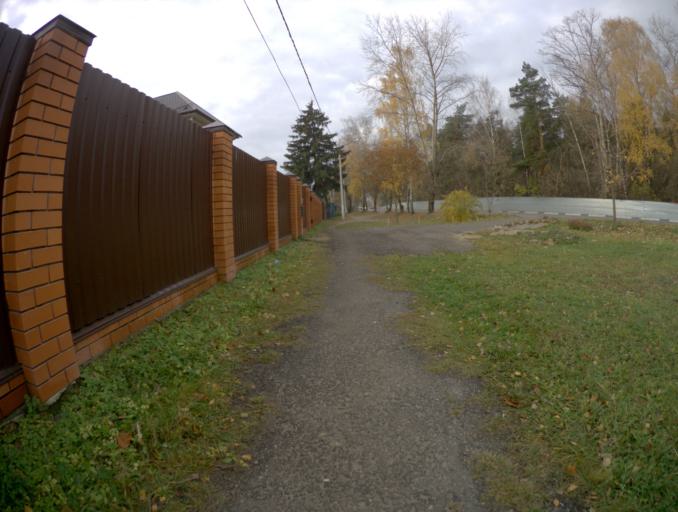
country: RU
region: Moskovskaya
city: Orekhovo-Zuyevo
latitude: 55.8050
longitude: 38.9587
